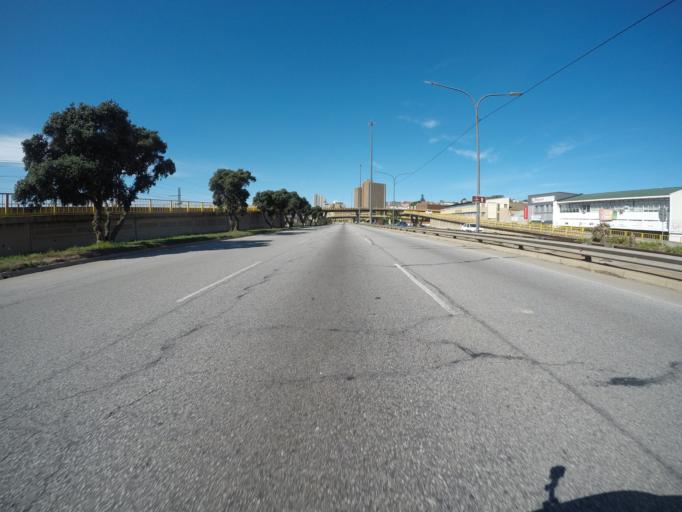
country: ZA
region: Eastern Cape
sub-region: Nelson Mandela Bay Metropolitan Municipality
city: Port Elizabeth
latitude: -33.9507
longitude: 25.6124
